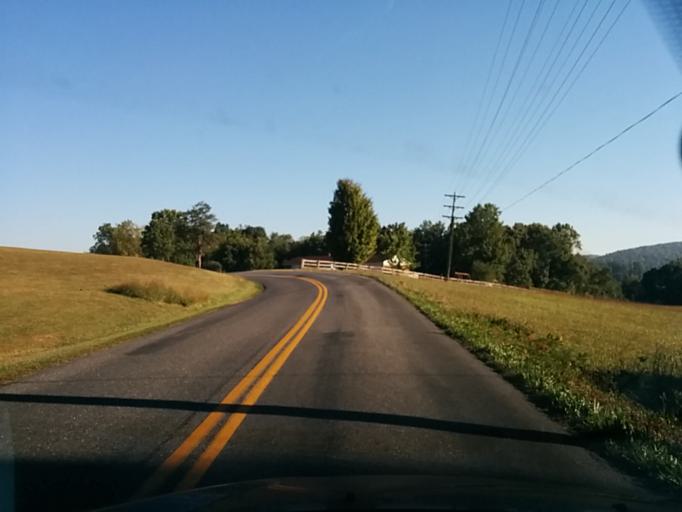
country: US
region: Virginia
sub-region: City of Lexington
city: Lexington
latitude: 37.7456
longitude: -79.5423
